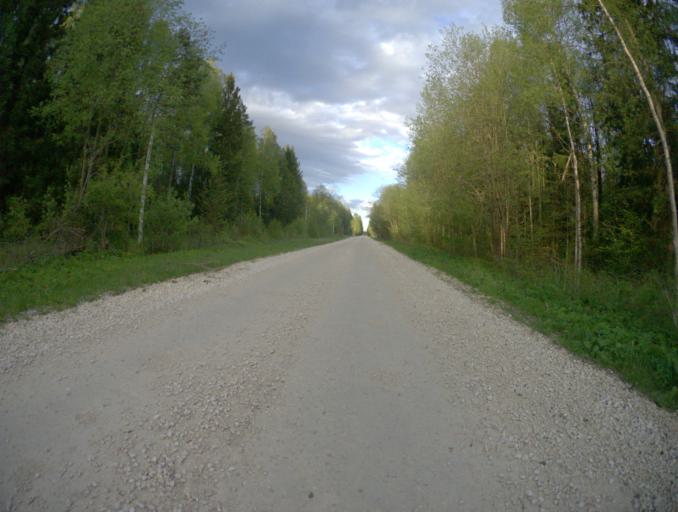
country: RU
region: Vladimir
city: Anopino
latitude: 55.7089
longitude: 40.6355
